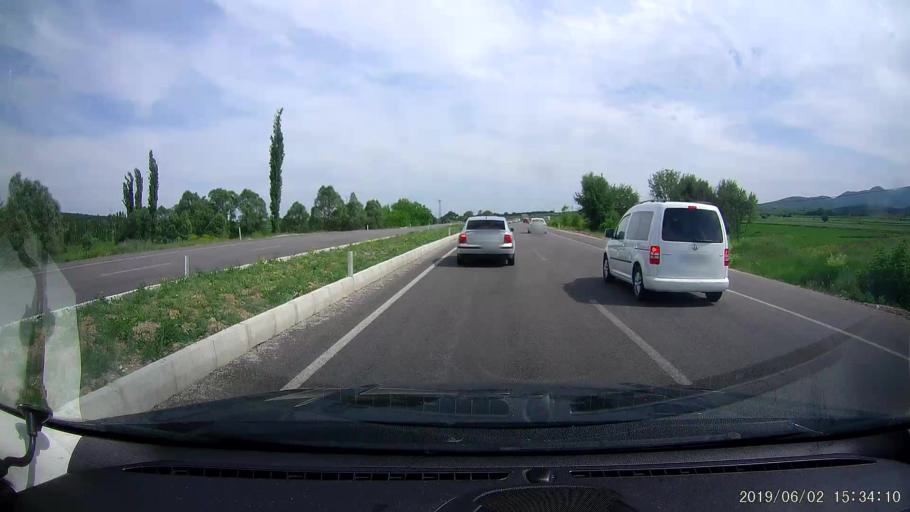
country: TR
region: Amasya
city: Saraycik
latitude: 40.9148
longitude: 35.1720
